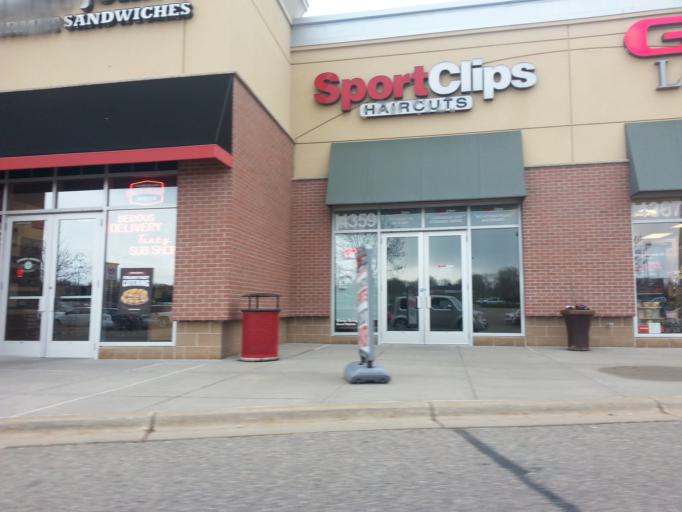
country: US
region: Minnesota
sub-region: Scott County
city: Prior Lake
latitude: 44.7431
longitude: -93.3773
